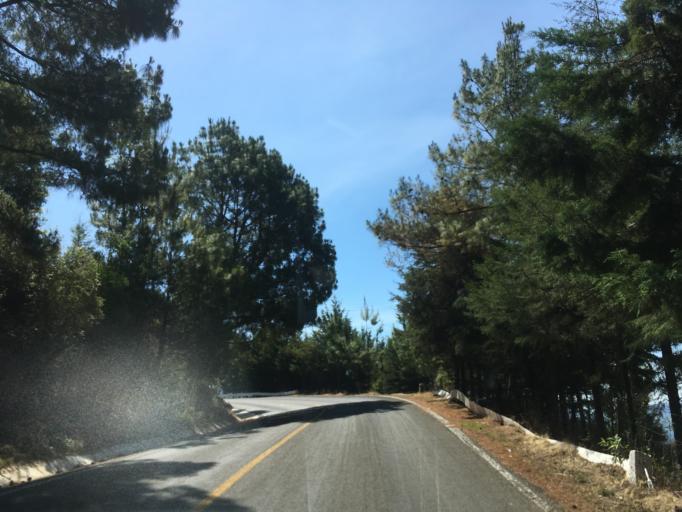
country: MX
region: Michoacan
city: Tzitzio
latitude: 19.6741
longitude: -100.9069
